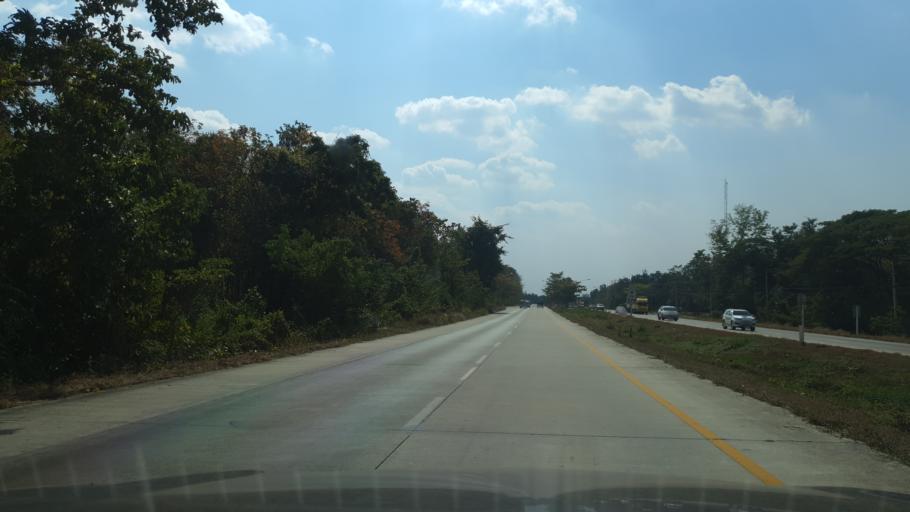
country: TH
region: Lampang
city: Mae Phrik
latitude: 17.3118
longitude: 99.1494
